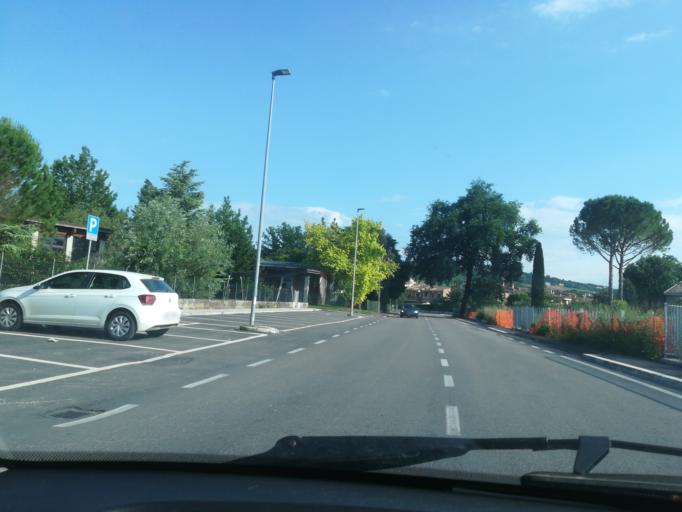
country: IT
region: The Marches
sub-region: Provincia di Macerata
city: Villa Potenza
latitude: 43.3230
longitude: 13.4241
